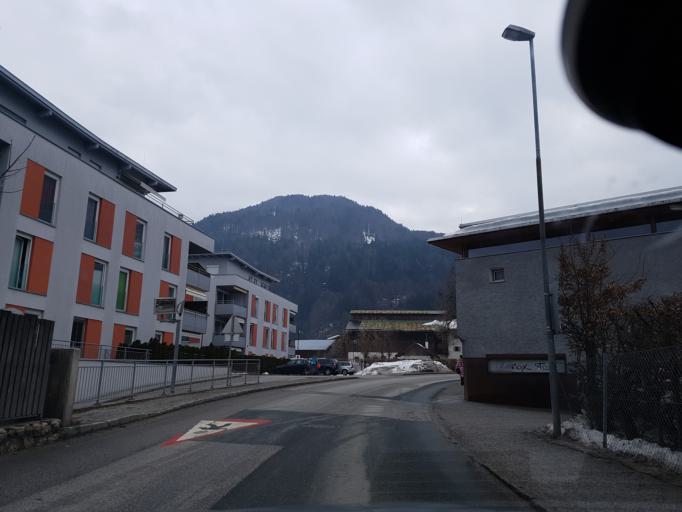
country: AT
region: Tyrol
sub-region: Politischer Bezirk Kufstein
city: Worgl
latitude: 47.4831
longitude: 12.0680
